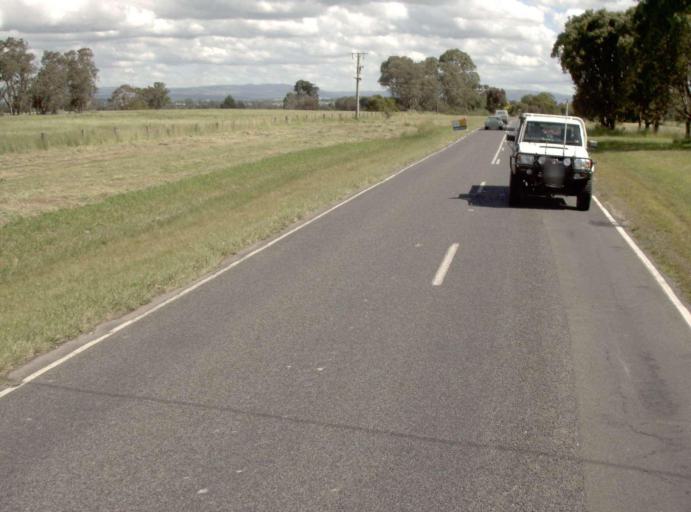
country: AU
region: Victoria
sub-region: Latrobe
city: Traralgon
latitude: -38.1480
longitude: 146.5234
